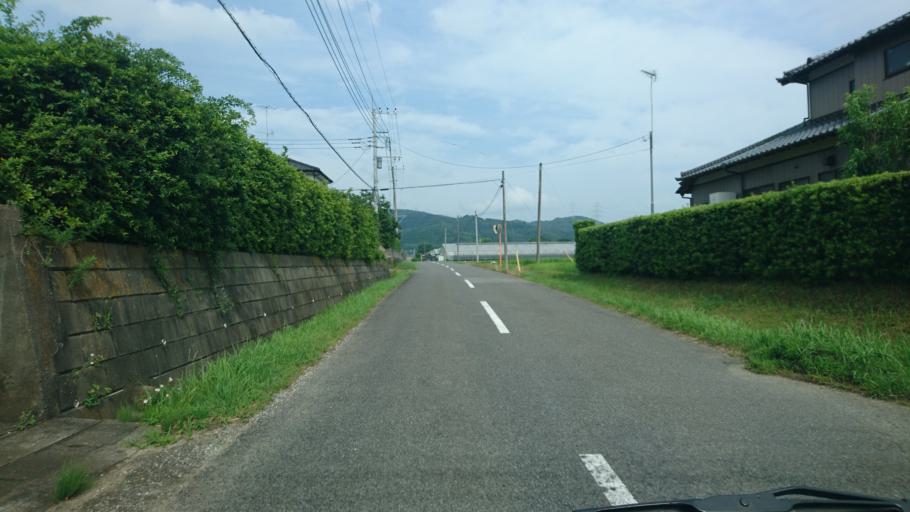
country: JP
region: Chiba
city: Kimitsu
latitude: 35.2935
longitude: 139.9826
